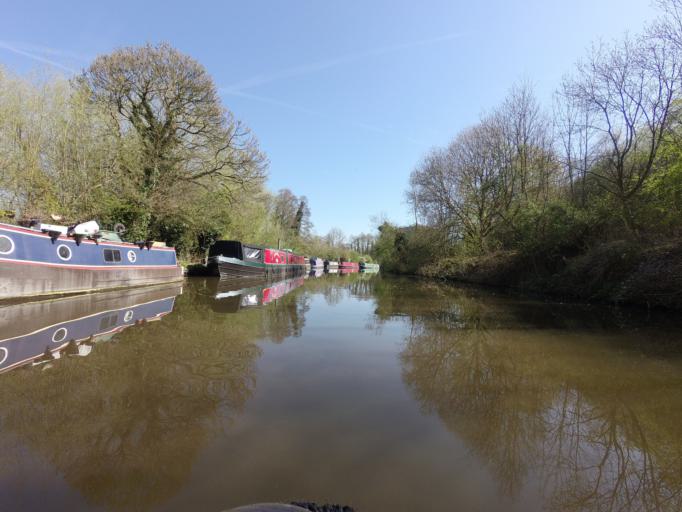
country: GB
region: England
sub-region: Hertfordshire
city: Rickmansworth
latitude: 51.6269
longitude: -0.4927
